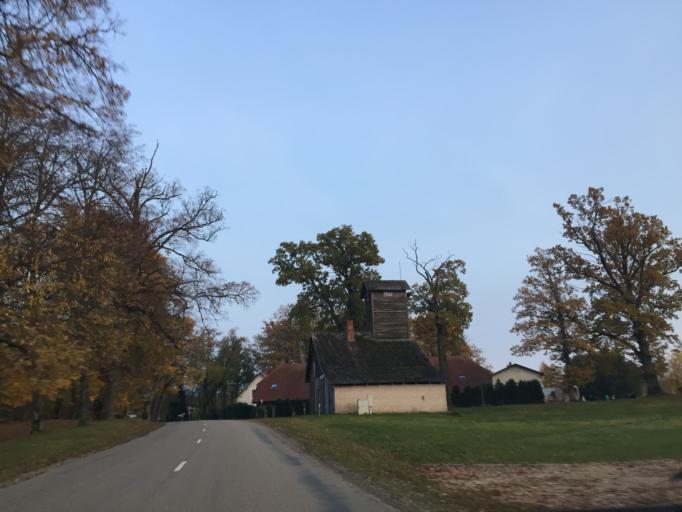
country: LV
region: Cesu Rajons
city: Cesis
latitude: 57.3132
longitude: 25.1556
